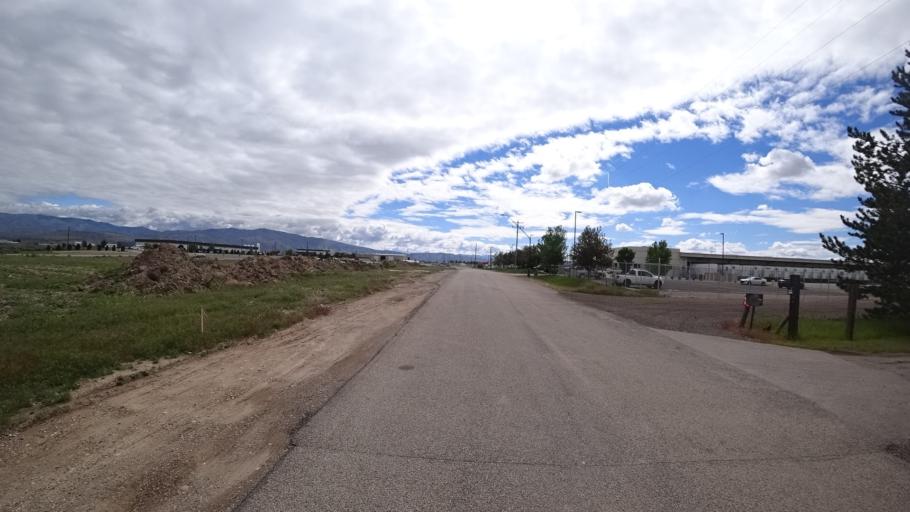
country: US
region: Idaho
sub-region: Ada County
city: Boise
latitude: 43.5461
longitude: -116.1957
